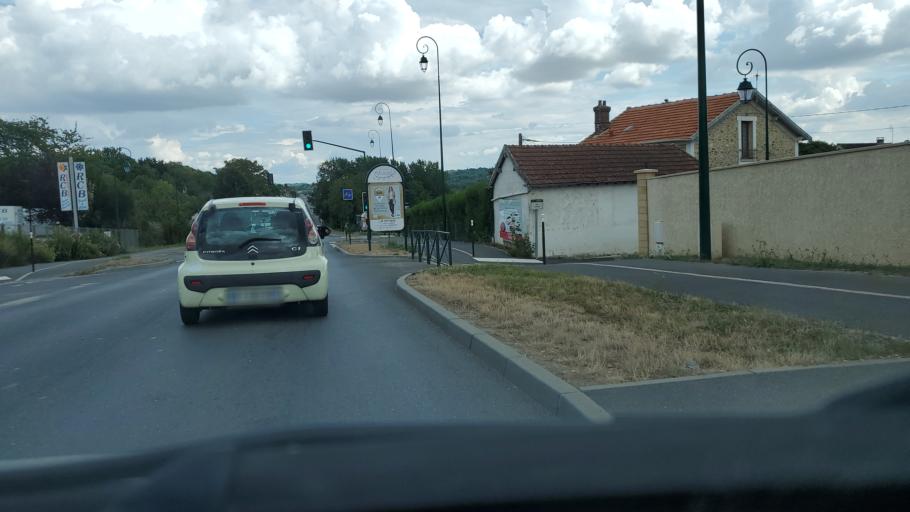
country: FR
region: Ile-de-France
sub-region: Departement de Seine-et-Marne
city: Mouroux
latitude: 48.8241
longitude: 3.0403
